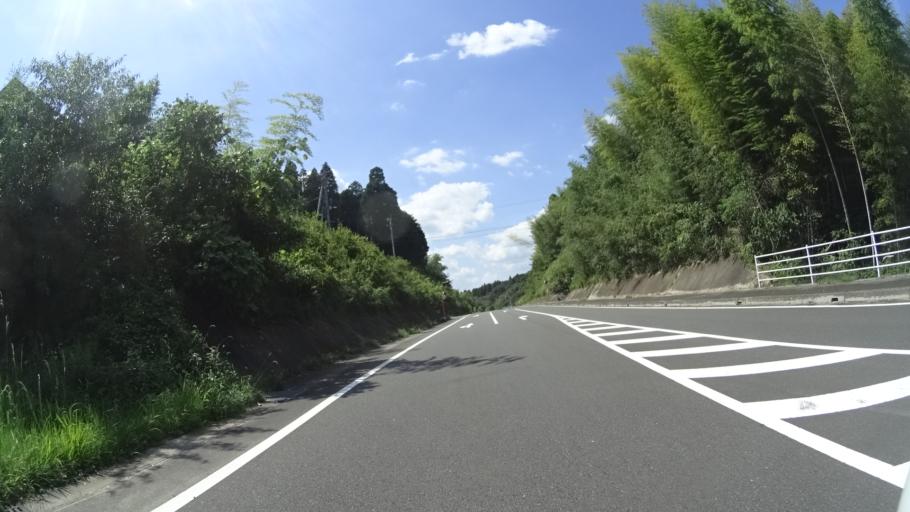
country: JP
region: Kagoshima
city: Kajiki
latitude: 31.8131
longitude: 130.6974
